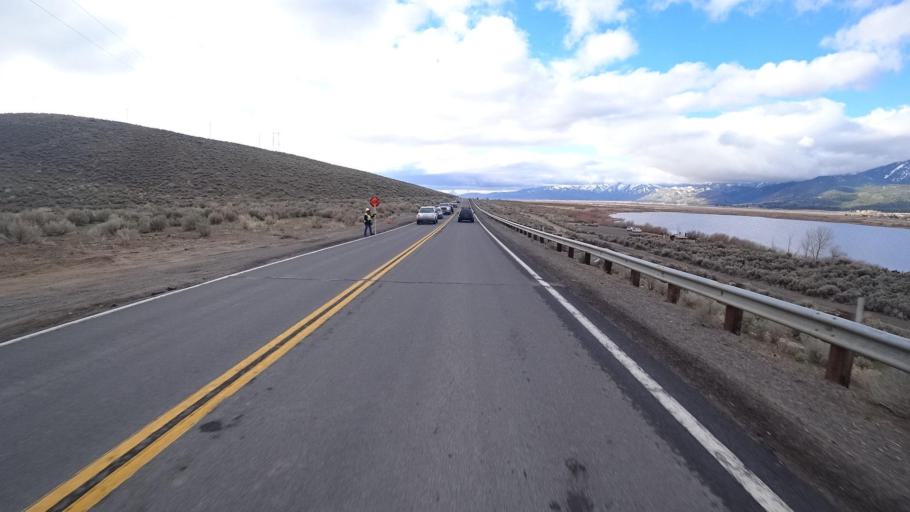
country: US
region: Nevada
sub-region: Storey County
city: Virginia City
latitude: 39.3279
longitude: -119.7915
